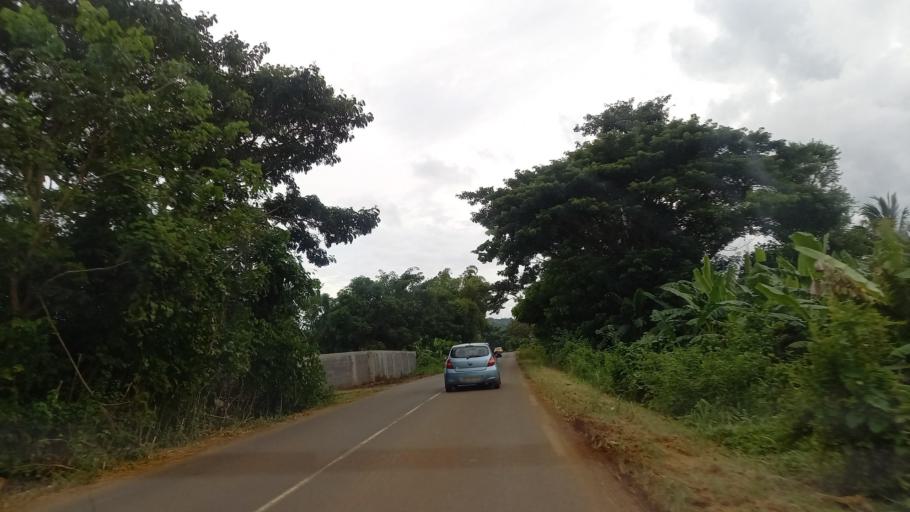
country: YT
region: Chirongui
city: Chirongui
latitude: -12.9074
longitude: 45.1576
